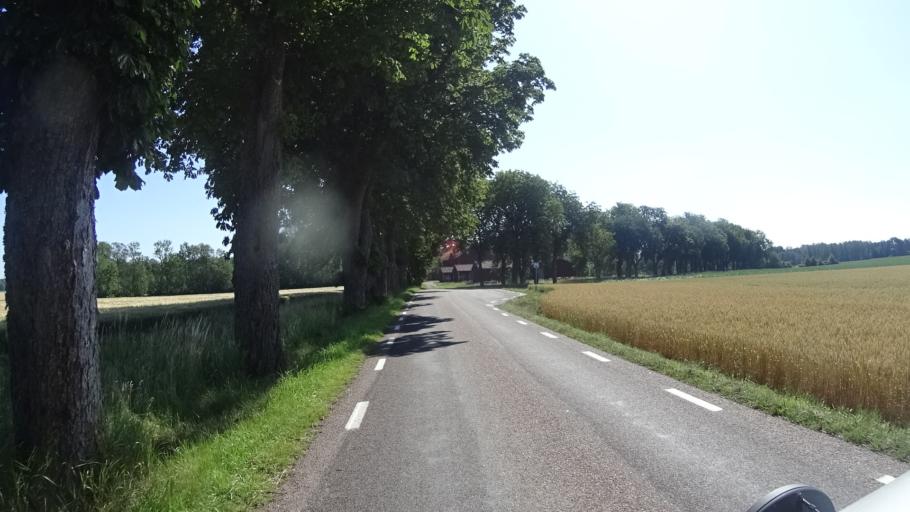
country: SE
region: OEstergoetland
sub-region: Vadstena Kommun
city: Herrestad
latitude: 58.3230
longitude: 14.8350
